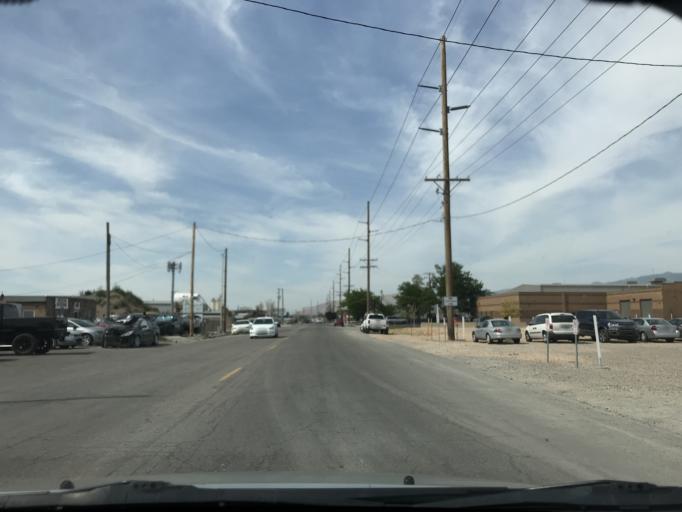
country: US
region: Utah
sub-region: Salt Lake County
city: Centerfield
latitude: 40.6950
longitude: -111.9055
